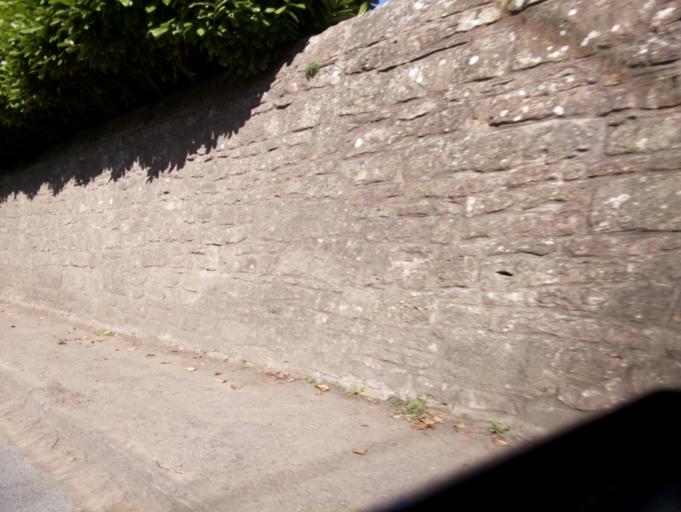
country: GB
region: England
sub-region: Herefordshire
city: Walford
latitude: 51.8815
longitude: -2.6008
